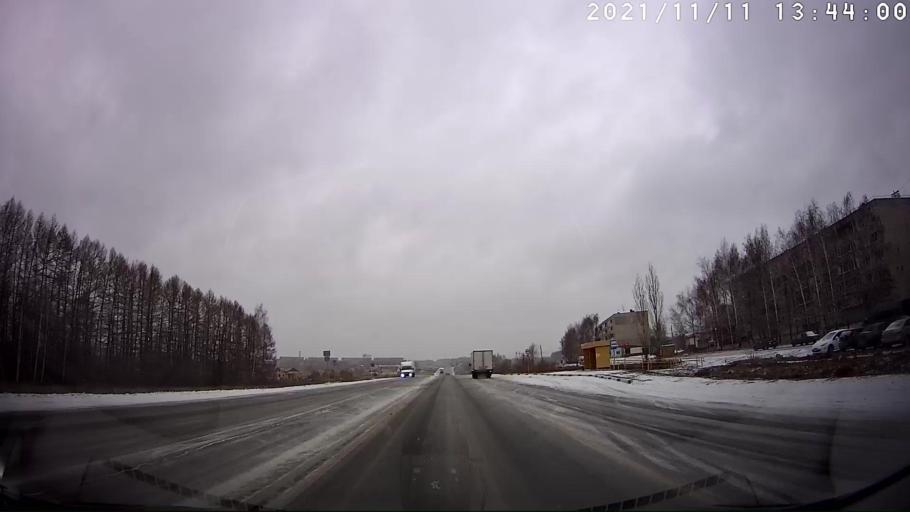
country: RU
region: Chuvashia
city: Kanash
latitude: 55.4915
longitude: 47.4765
